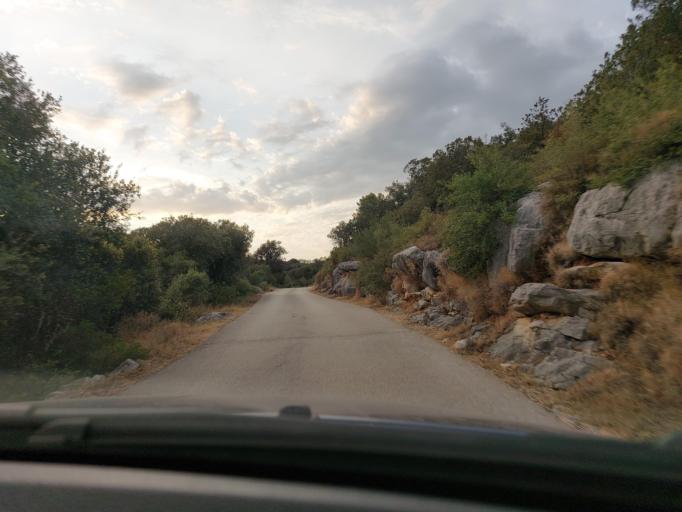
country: HR
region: Dubrovacko-Neretvanska
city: Smokvica
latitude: 42.7598
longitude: 16.9165
